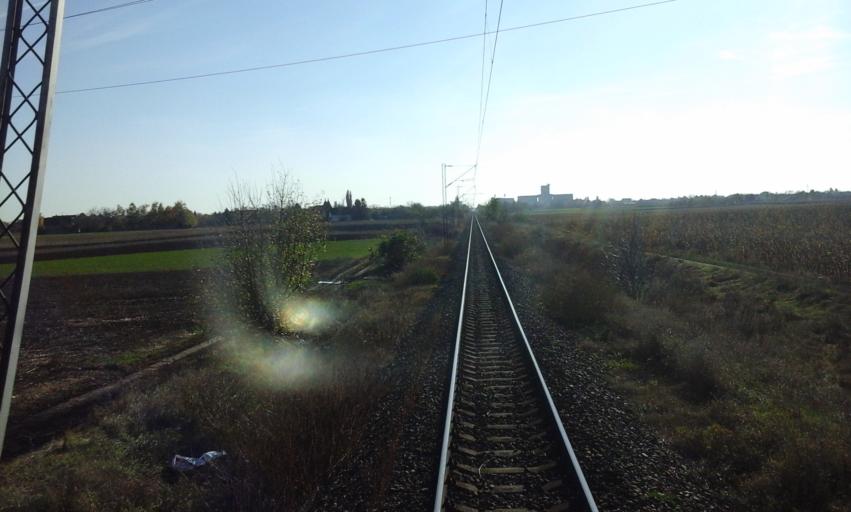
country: RS
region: Autonomna Pokrajina Vojvodina
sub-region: Severnobacki Okrug
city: Backa Topola
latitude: 45.8331
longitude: 19.6519
